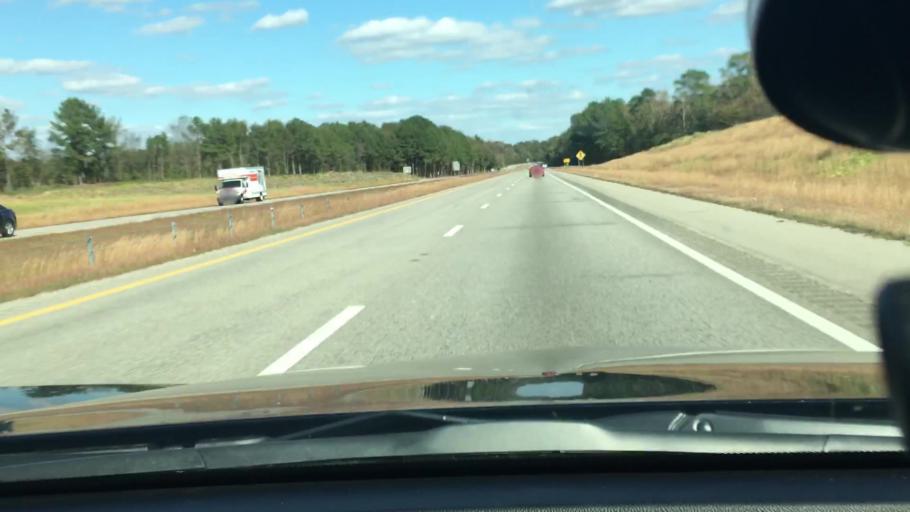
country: US
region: North Carolina
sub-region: Wilson County
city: Wilson
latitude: 35.6751
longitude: -77.8567
